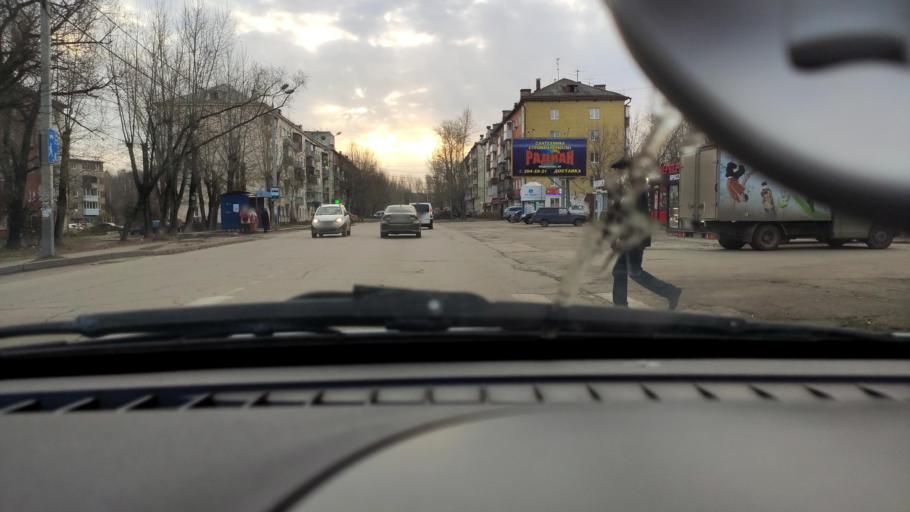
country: RU
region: Perm
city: Perm
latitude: 58.1043
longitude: 56.3853
